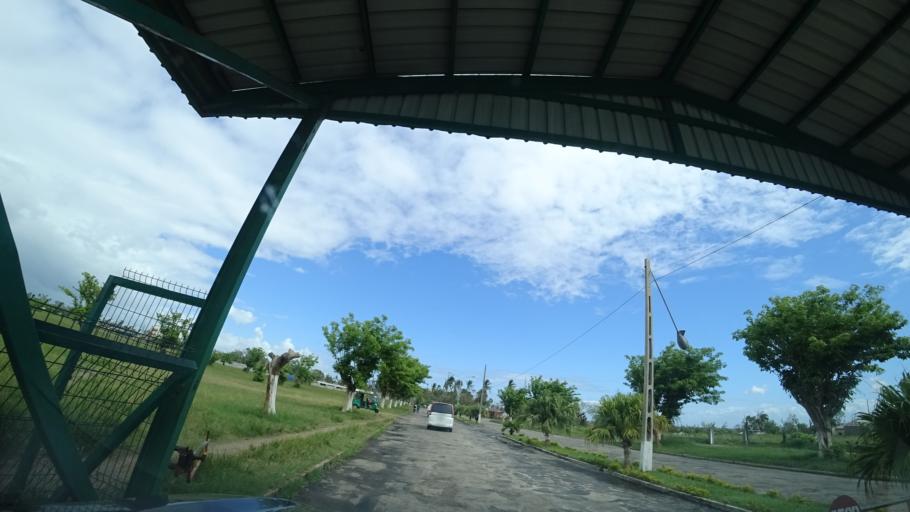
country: MZ
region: Sofala
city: Beira
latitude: -19.7999
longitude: 34.9002
